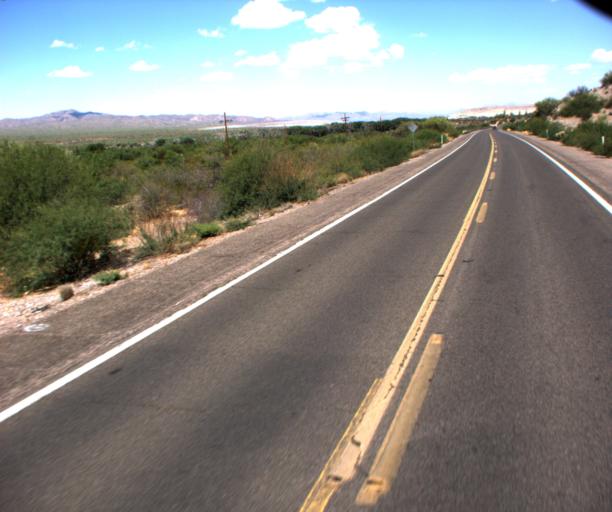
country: US
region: Arizona
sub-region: Pinal County
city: Kearny
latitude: 32.9659
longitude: -110.7554
